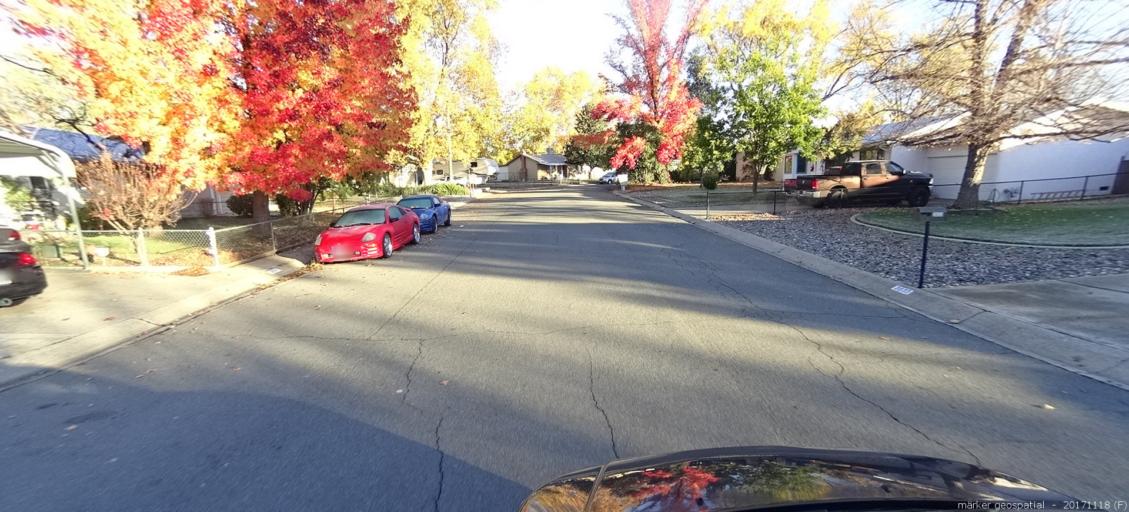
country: US
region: California
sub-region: Shasta County
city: Cottonwood
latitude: 40.3929
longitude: -122.2903
